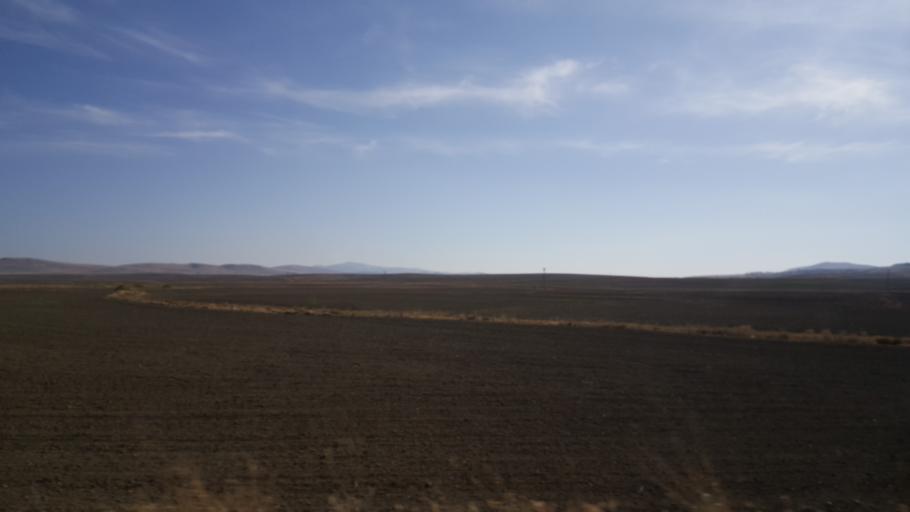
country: TR
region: Ankara
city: Yenice
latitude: 39.3764
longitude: 32.7429
